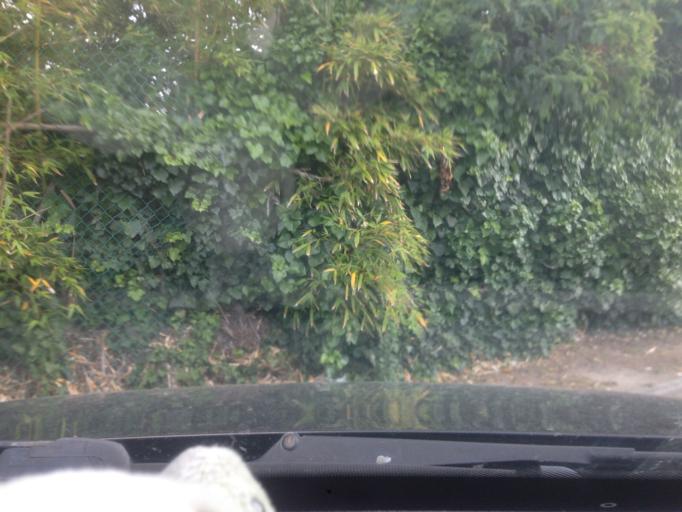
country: FR
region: Brittany
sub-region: Departement du Morbihan
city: Carnac
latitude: 47.5858
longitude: -3.0844
